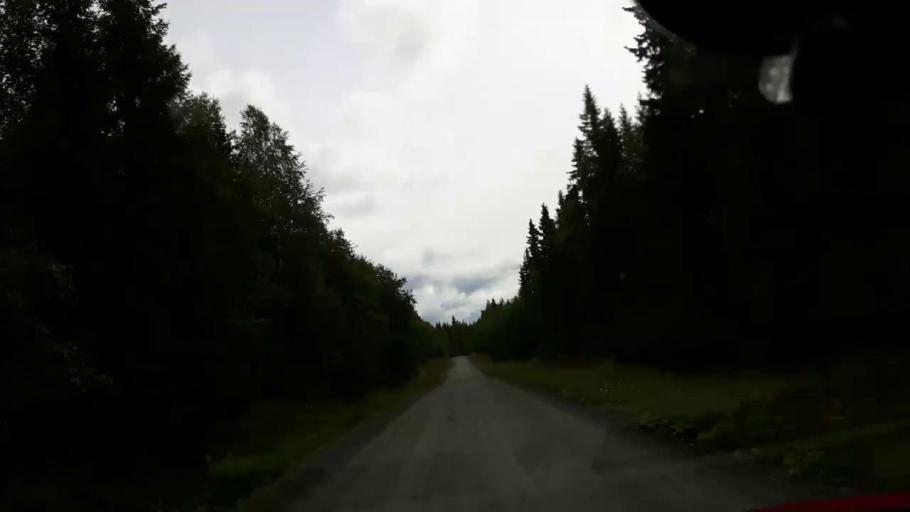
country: SE
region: Jaemtland
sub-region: Krokoms Kommun
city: Valla
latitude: 63.6599
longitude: 13.9716
